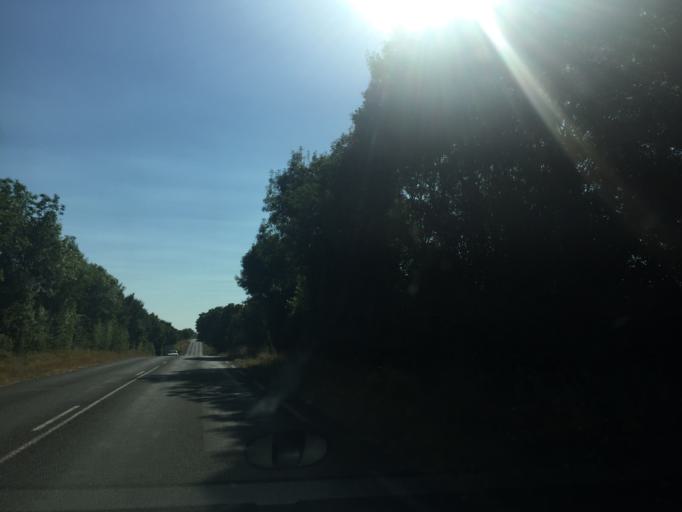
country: FR
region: Poitou-Charentes
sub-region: Departement des Deux-Sevres
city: Melle
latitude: 46.2323
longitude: -0.1181
